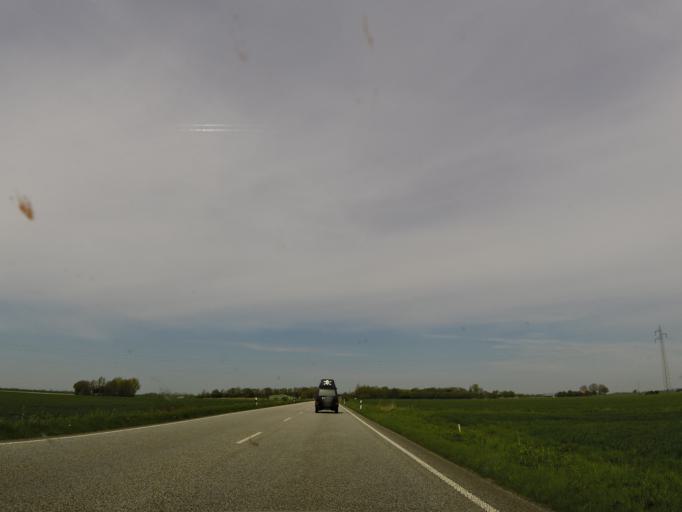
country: DE
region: Schleswig-Holstein
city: Groven
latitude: 54.2947
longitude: 8.9752
